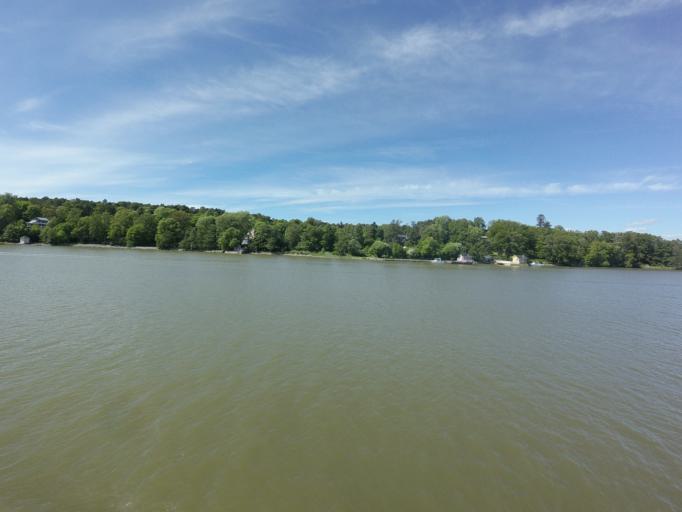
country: FI
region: Varsinais-Suomi
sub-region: Turku
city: Raisio
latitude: 60.4231
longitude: 22.1793
